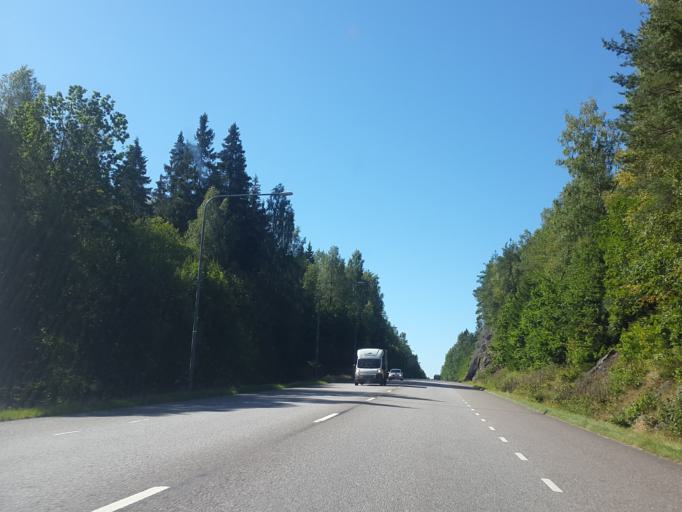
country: SE
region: Vaestra Goetaland
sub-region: Boras Kommun
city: Boras
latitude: 57.7670
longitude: 12.9717
